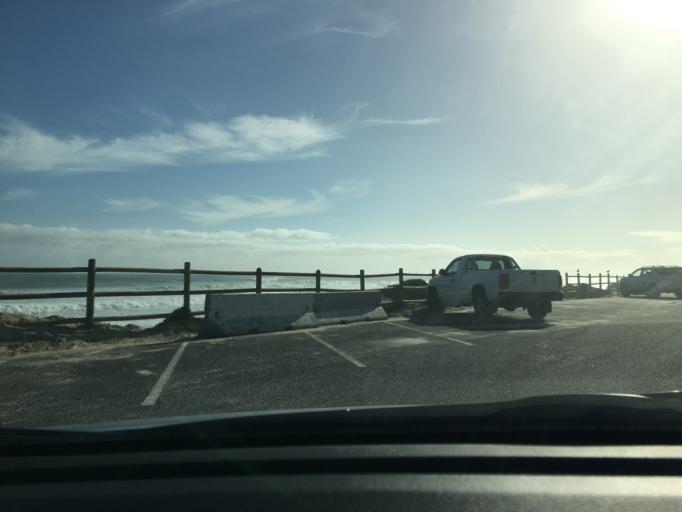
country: ZA
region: Western Cape
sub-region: City of Cape Town
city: Sunset Beach
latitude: -33.8194
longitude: 18.4749
